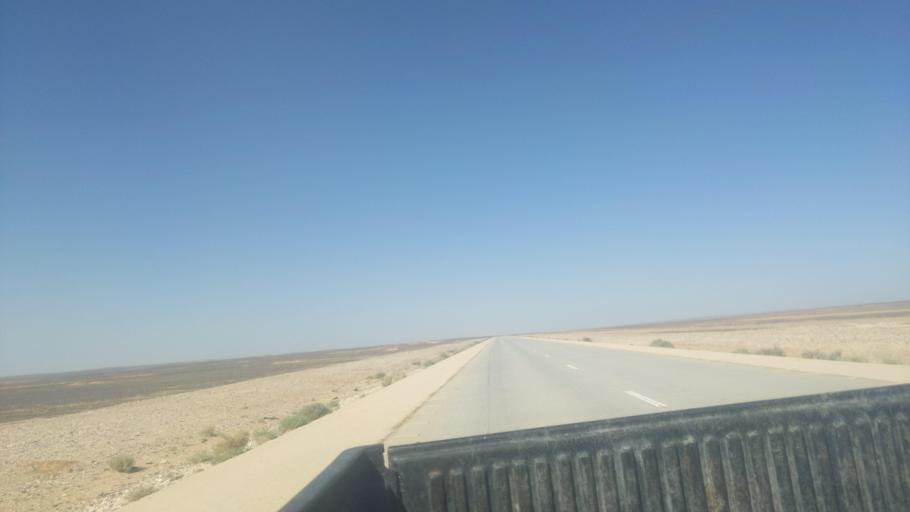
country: JO
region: Amman
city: Al Azraq ash Shamali
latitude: 31.4538
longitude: 36.7786
